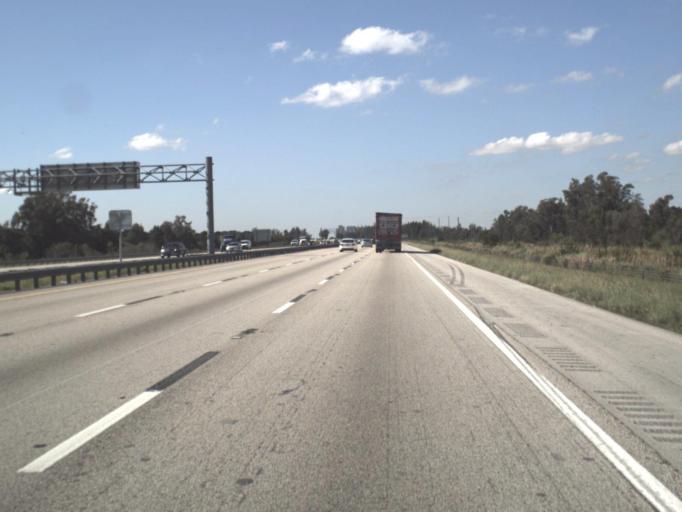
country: US
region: Florida
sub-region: Miami-Dade County
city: Palm Springs North
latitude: 25.9375
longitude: -80.3653
